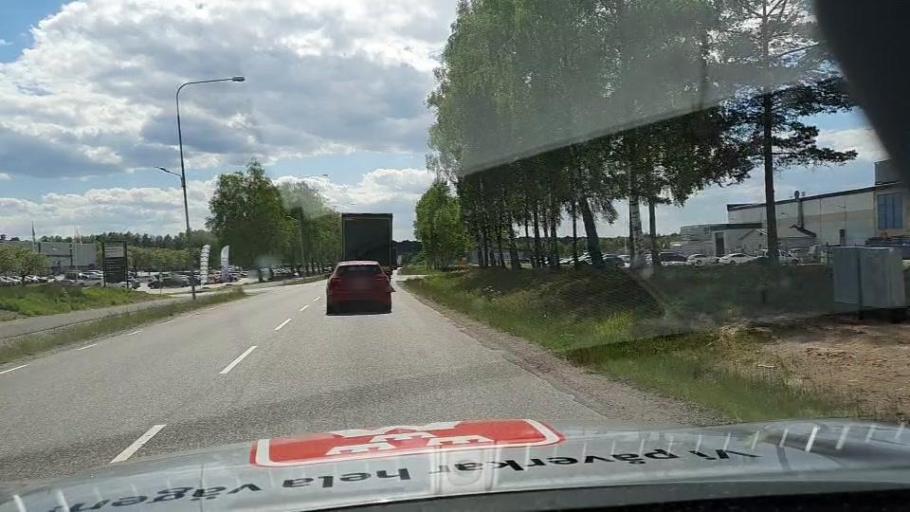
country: SE
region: Kronoberg
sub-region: Ljungby Kommun
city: Ljungby
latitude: 56.8496
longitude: 13.9274
